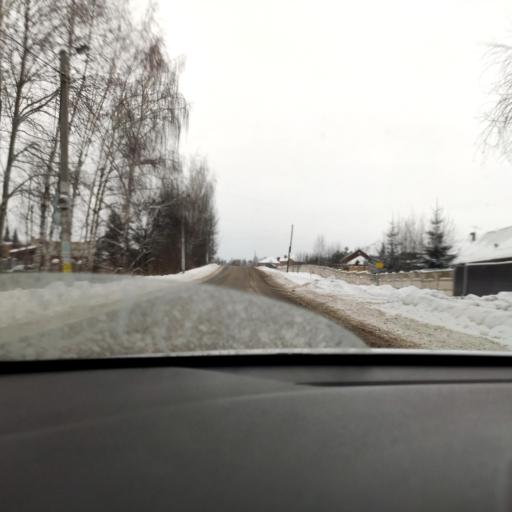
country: RU
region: Tatarstan
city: Osinovo
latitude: 55.8561
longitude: 48.8209
